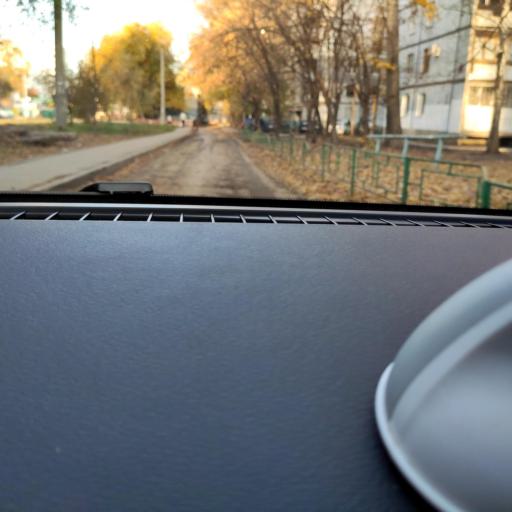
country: RU
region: Samara
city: Samara
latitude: 53.2369
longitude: 50.2140
